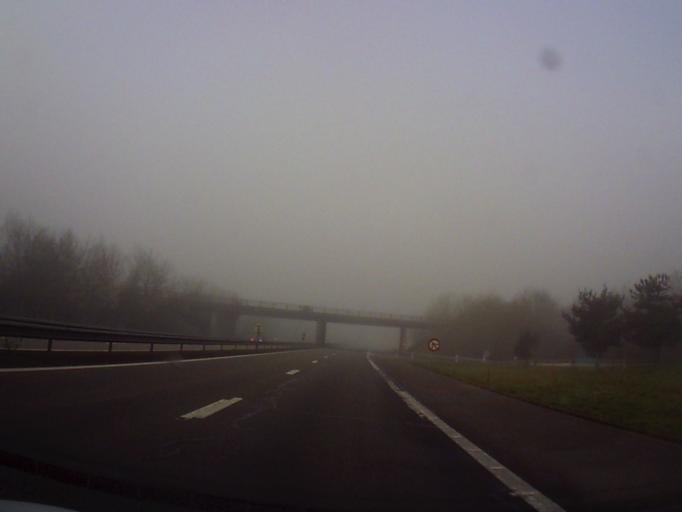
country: FR
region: Brittany
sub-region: Departement d'Ille-et-Vilaine
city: Mordelles
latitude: 48.0681
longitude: -1.8210
